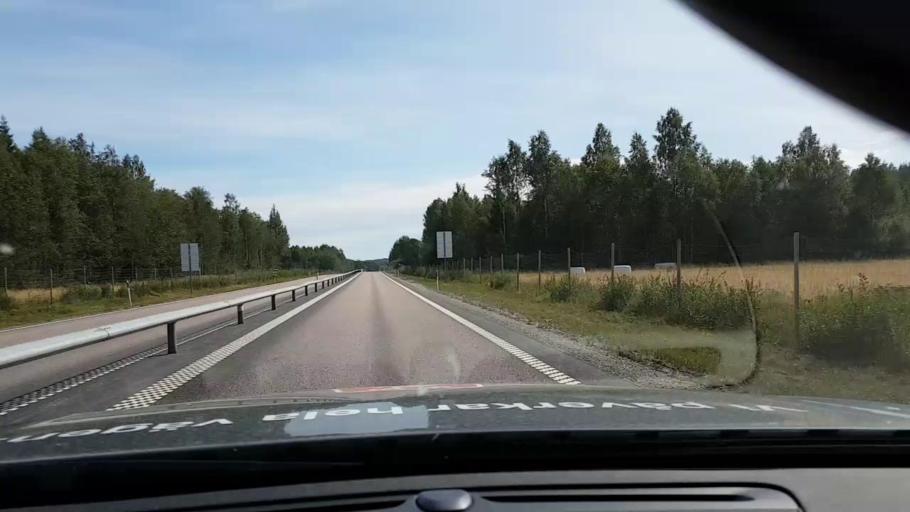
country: SE
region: Vaesternorrland
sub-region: OErnskoeldsviks Kommun
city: Ornskoldsvik
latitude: 63.3069
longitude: 18.8475
